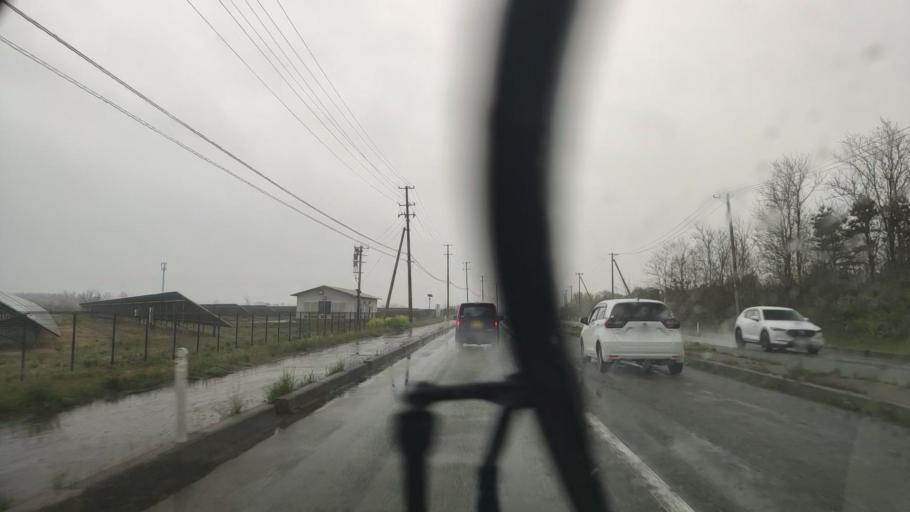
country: JP
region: Akita
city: Tenno
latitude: 39.8920
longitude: 139.9597
